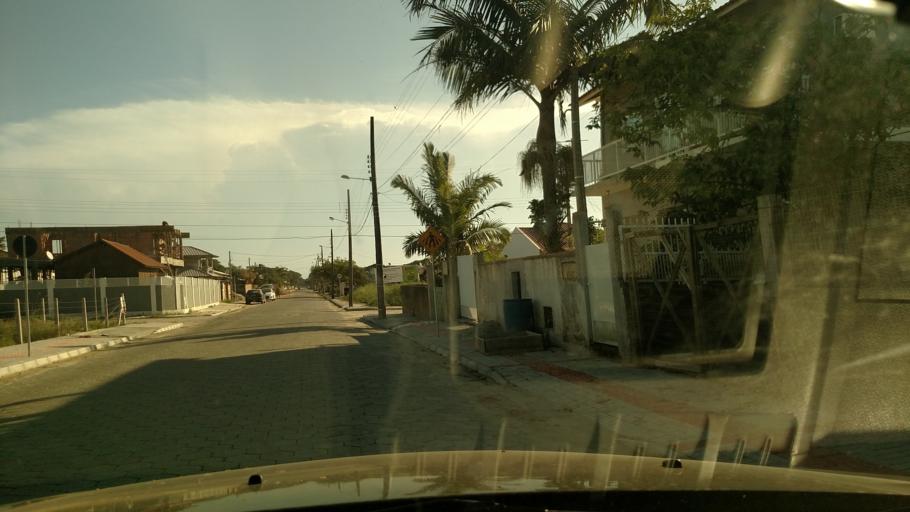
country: BR
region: Santa Catarina
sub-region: Porto Belo
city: Porto Belo
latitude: -27.1765
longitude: -48.5060
